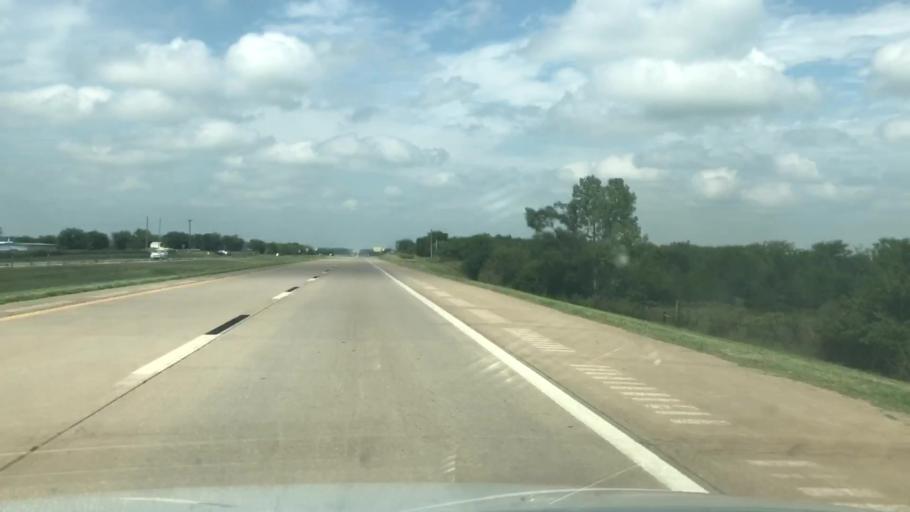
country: US
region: Oklahoma
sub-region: Osage County
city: Skiatook
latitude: 36.4212
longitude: -95.9203
